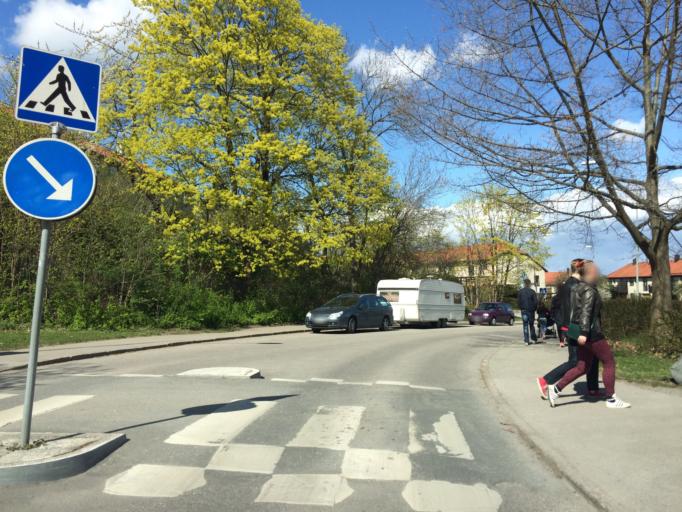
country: SE
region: Stockholm
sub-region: Stockholms Kommun
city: Bromma
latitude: 59.3058
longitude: 17.9753
